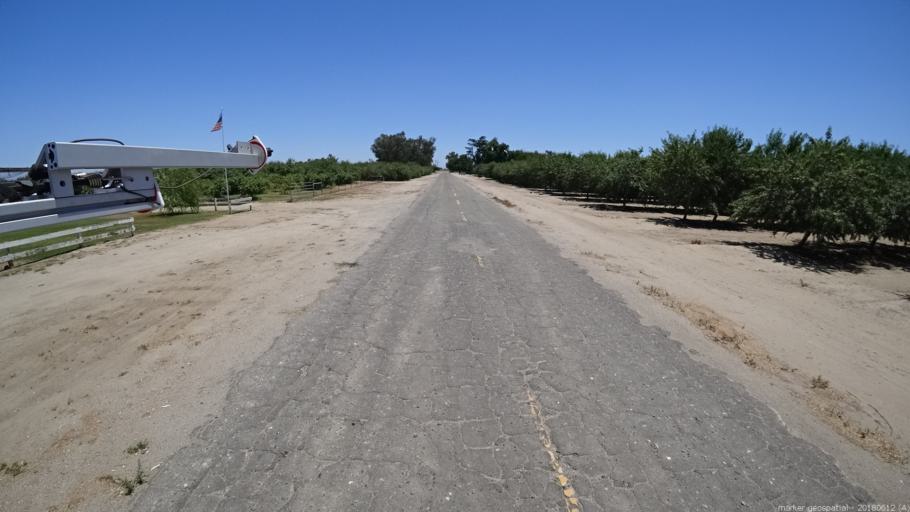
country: US
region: California
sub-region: Madera County
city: Chowchilla
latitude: 37.0983
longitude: -120.2720
